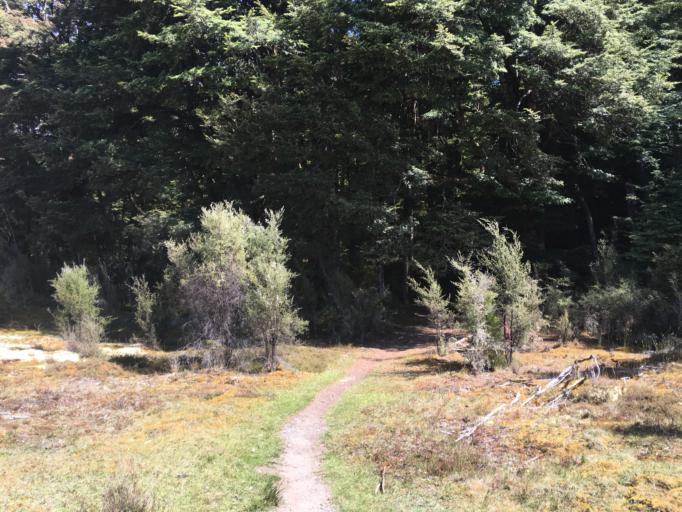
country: NZ
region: Southland
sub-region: Southland District
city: Te Anau
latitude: -45.4863
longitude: 167.6852
